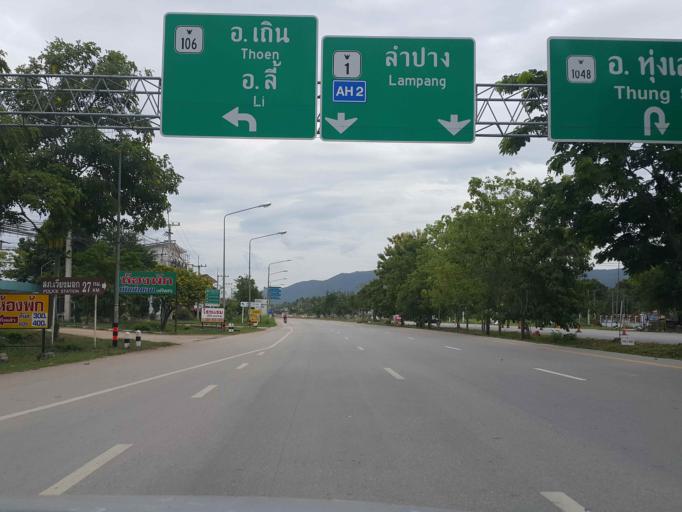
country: TH
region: Lampang
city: Thoen
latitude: 17.6263
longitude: 99.2377
